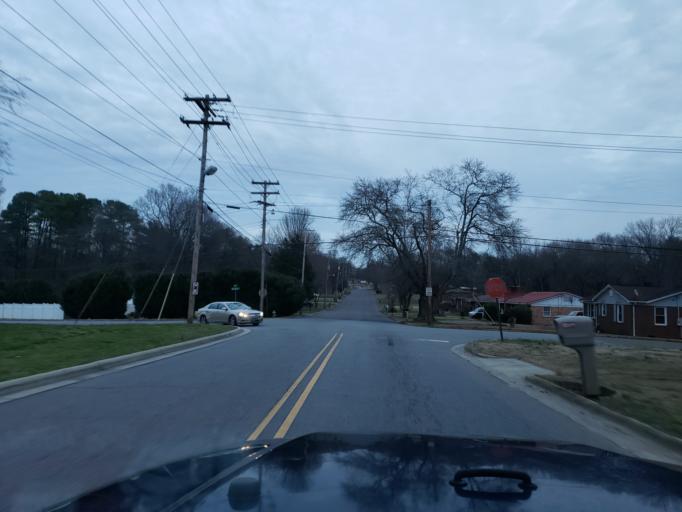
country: US
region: North Carolina
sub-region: Cleveland County
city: Shelby
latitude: 35.2774
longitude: -81.5257
